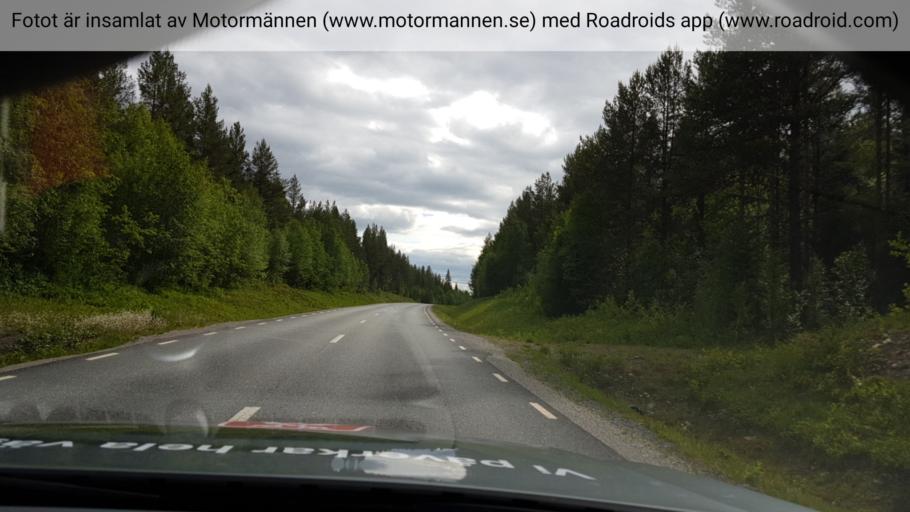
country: SE
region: Jaemtland
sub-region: Stroemsunds Kommun
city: Stroemsund
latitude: 63.9929
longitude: 15.5100
